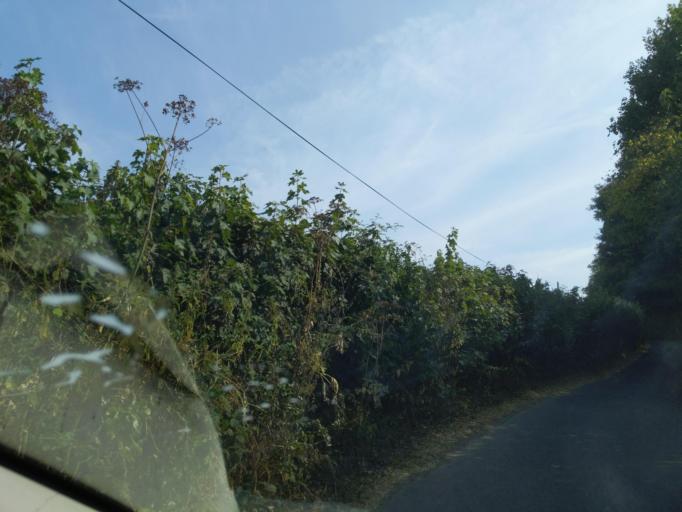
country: GB
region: England
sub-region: Devon
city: Winkleigh
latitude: 50.8777
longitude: -3.8723
